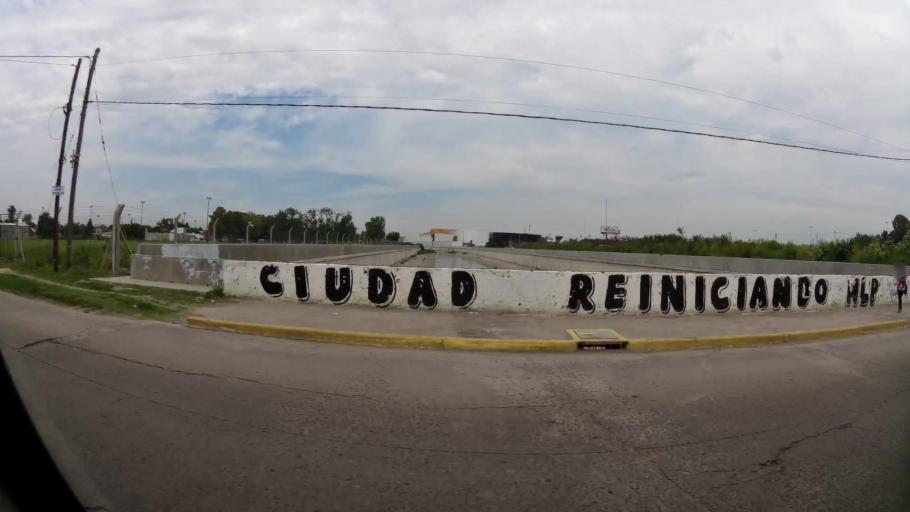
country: AR
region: Buenos Aires
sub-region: Partido de La Plata
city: La Plata
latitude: -34.9023
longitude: -57.9940
